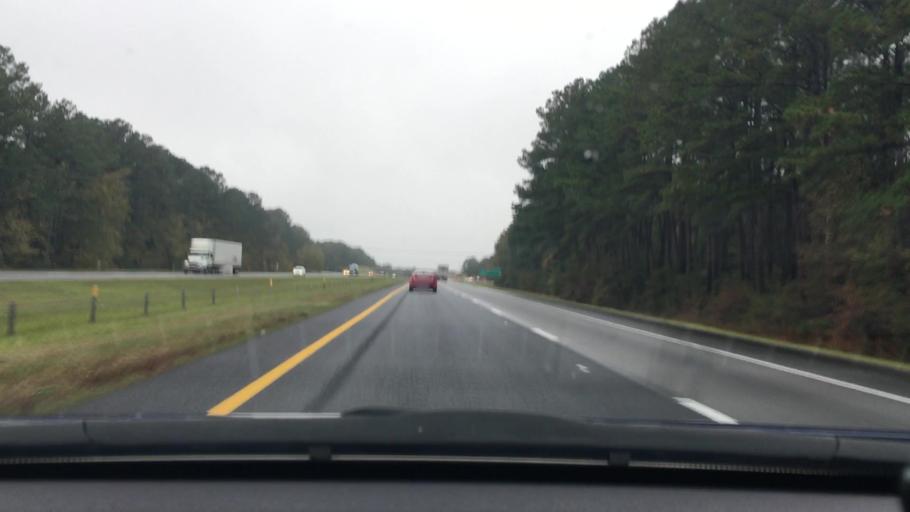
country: US
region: South Carolina
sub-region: Lee County
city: Bishopville
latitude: 34.1914
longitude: -80.1576
